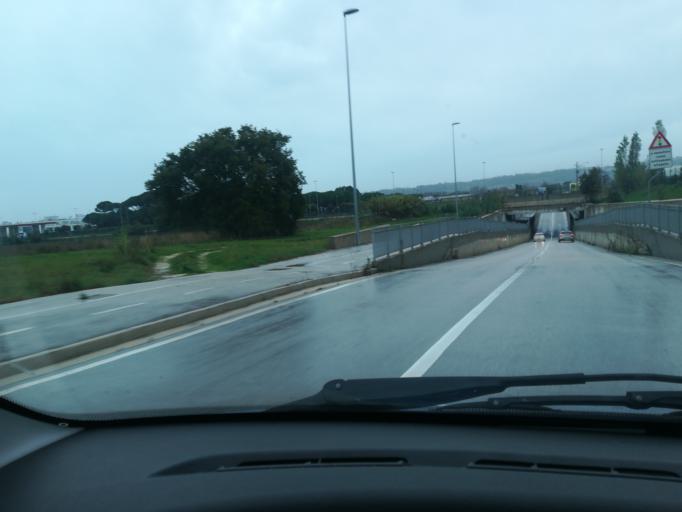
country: IT
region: The Marches
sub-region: Provincia di Macerata
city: Santa Maria Apparente
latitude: 43.2977
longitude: 13.7009
